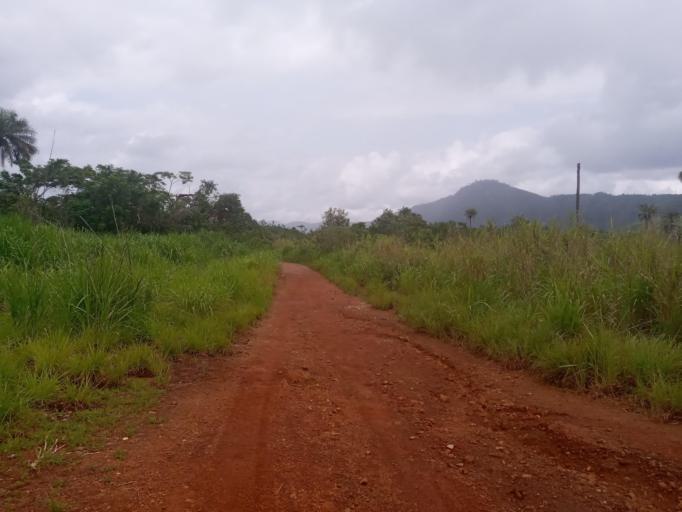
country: SL
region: Northern Province
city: Bumbuna
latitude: 8.9688
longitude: -11.7550
